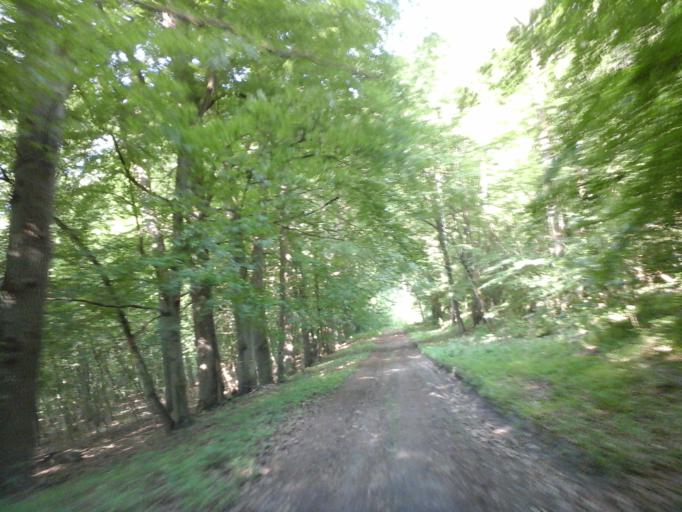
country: PL
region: West Pomeranian Voivodeship
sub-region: Powiat choszczenski
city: Recz
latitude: 53.3163
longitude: 15.5150
